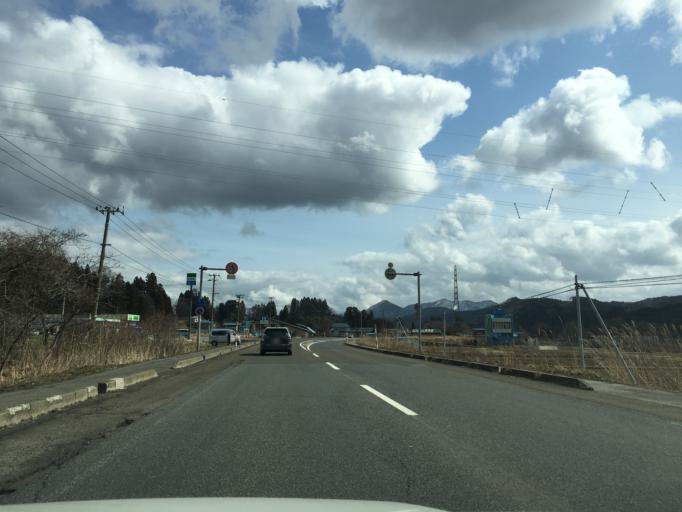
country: JP
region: Akita
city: Odate
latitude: 40.2286
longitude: 140.5971
